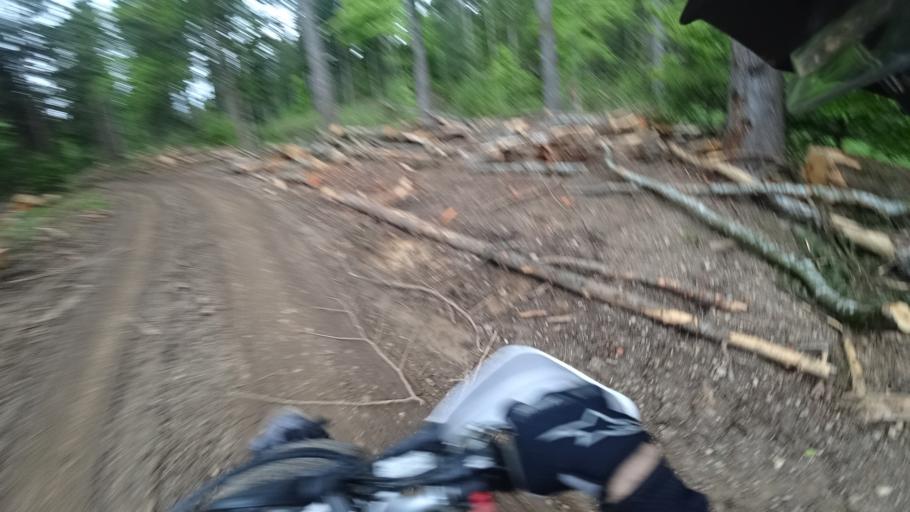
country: HR
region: Karlovacka
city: Plaski
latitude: 44.9524
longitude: 15.4151
